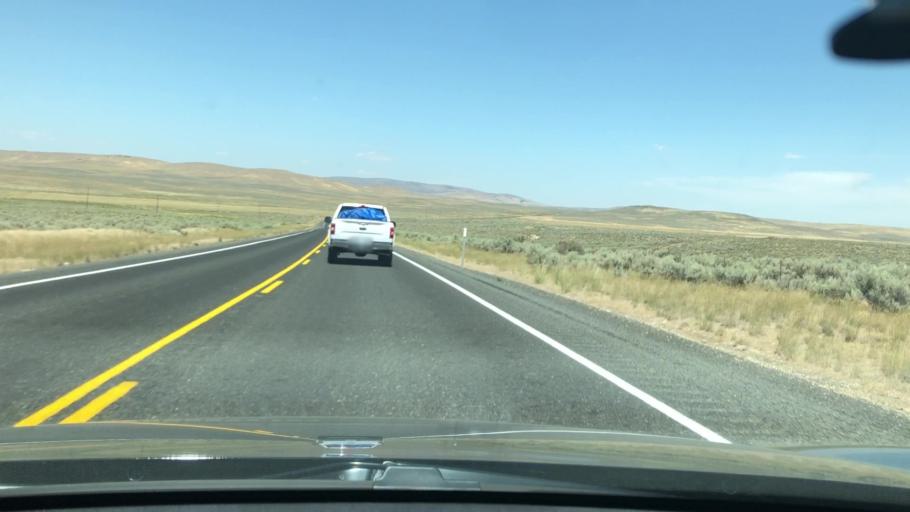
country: US
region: Idaho
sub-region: Owyhee County
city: Murphy
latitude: 43.0325
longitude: -117.0674
